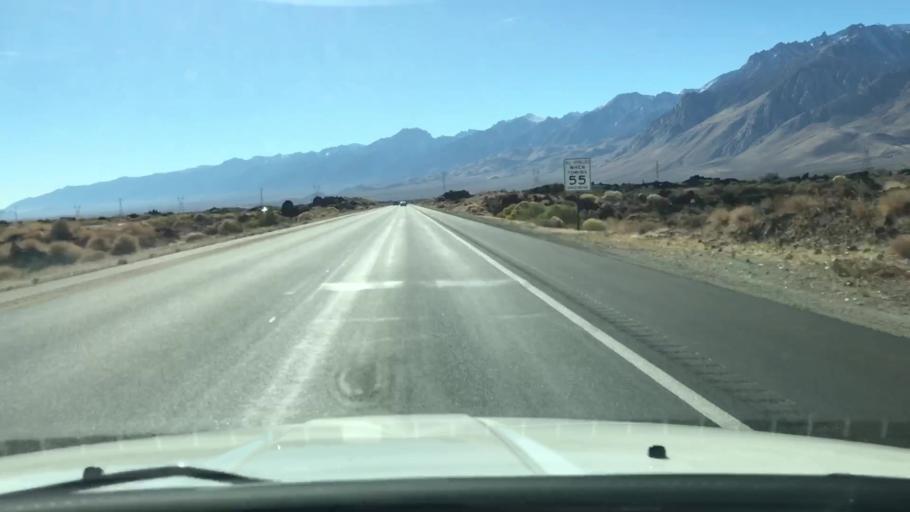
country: US
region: California
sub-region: Inyo County
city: Big Pine
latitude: 36.9885
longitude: -118.2350
